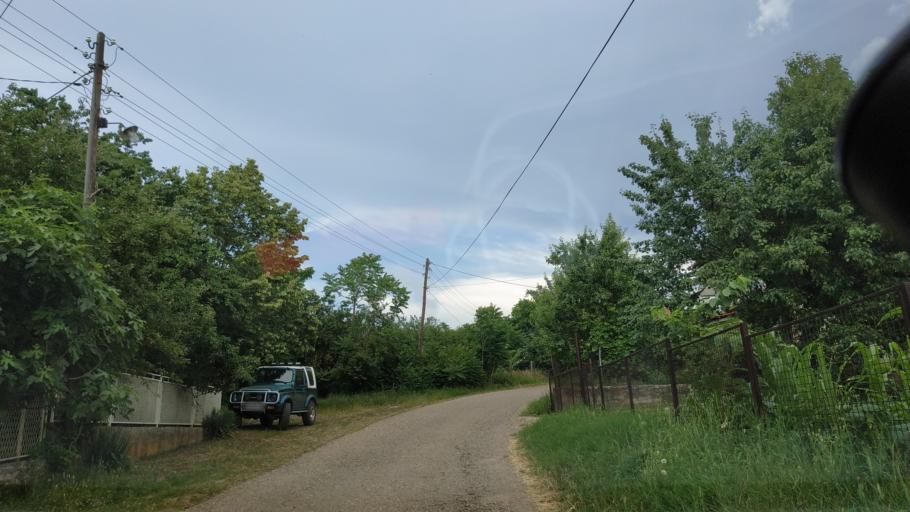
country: RS
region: Central Serbia
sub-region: Nisavski Okrug
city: Aleksinac
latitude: 43.6034
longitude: 21.6917
